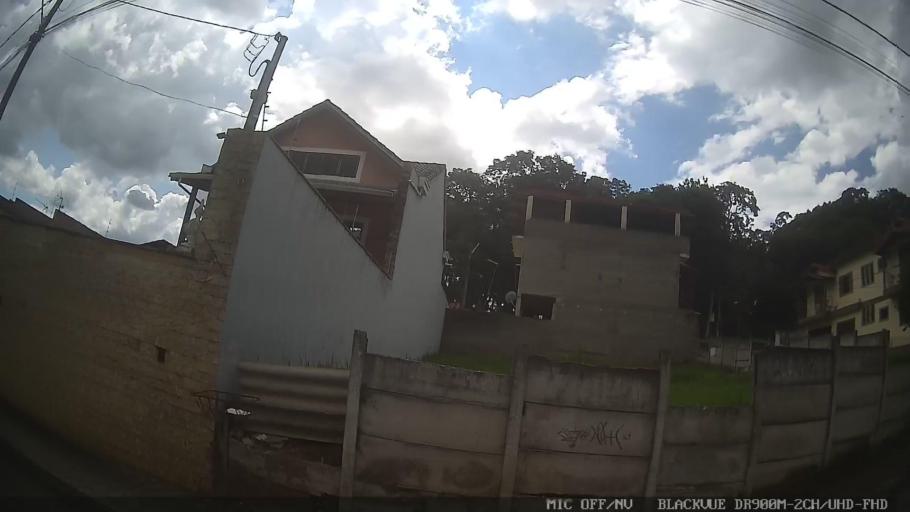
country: BR
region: Minas Gerais
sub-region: Extrema
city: Extrema
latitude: -22.8554
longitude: -46.3237
